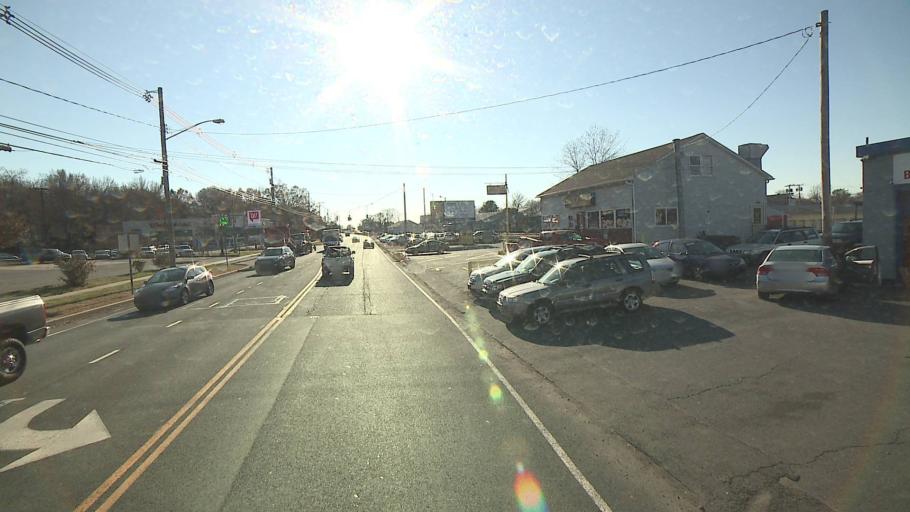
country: US
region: Connecticut
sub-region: New Haven County
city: Wallingford
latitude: 41.4522
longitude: -72.8267
